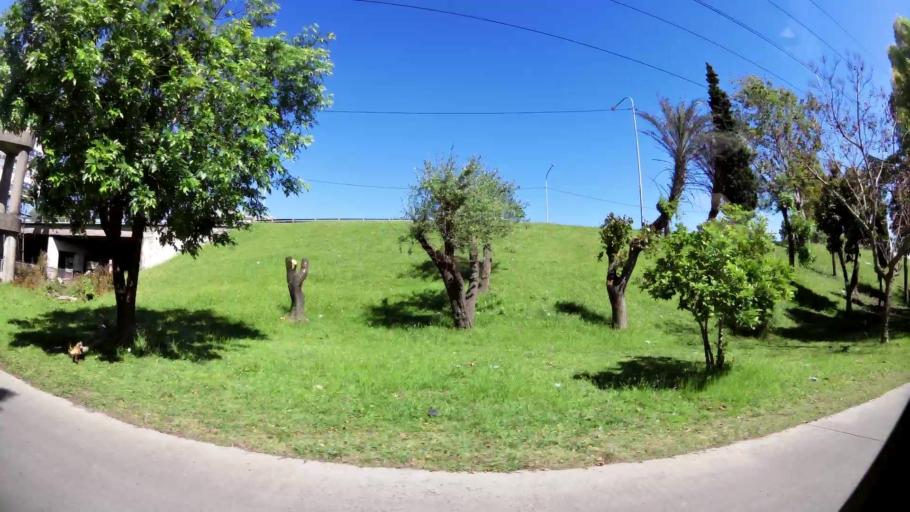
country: AR
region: Buenos Aires
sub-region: Partido de Quilmes
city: Quilmes
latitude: -34.7004
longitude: -58.3037
